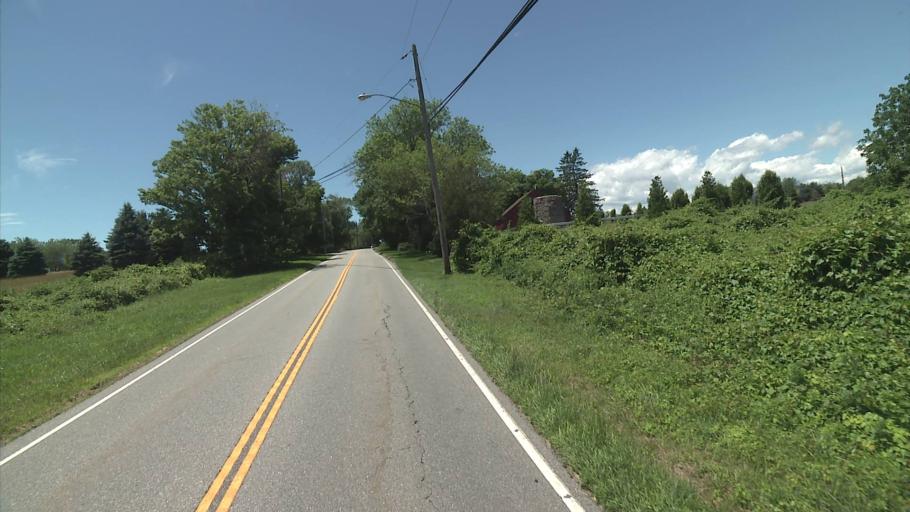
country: US
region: Connecticut
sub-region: New London County
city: Pawcatuck
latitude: 41.3824
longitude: -71.8845
